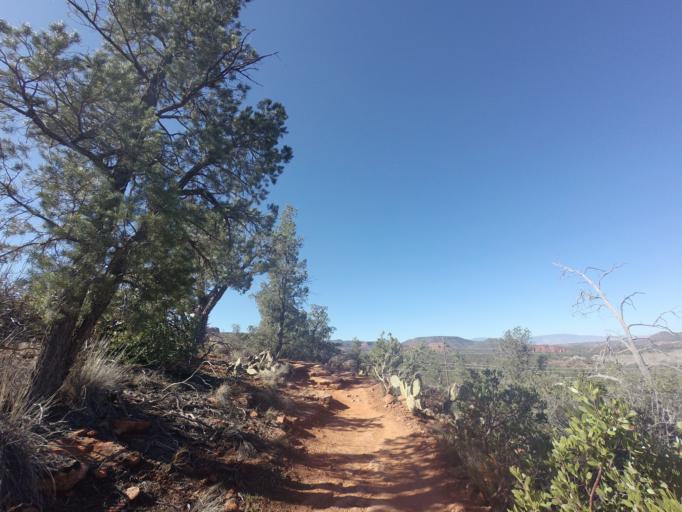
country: US
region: Arizona
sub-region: Yavapai County
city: West Sedona
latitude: 34.8156
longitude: -111.8073
